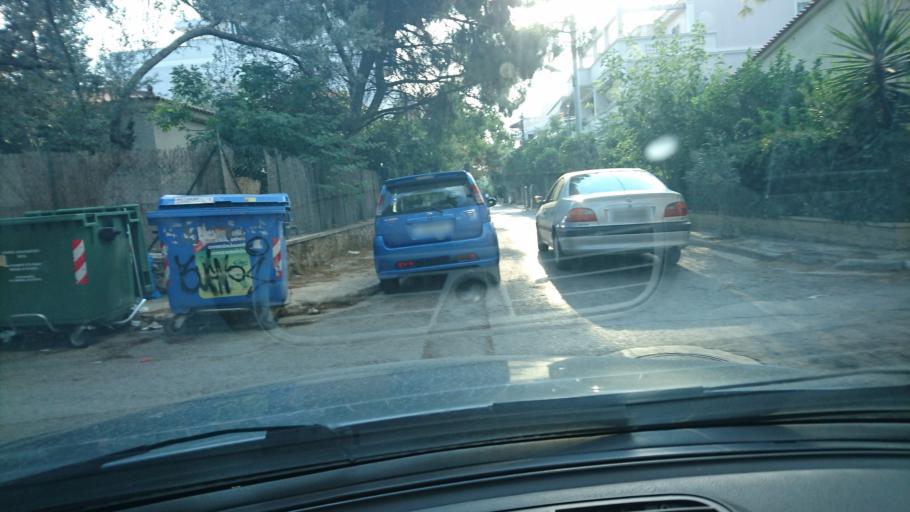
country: GR
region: Attica
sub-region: Nomarchia Athinas
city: Cholargos
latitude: 38.0078
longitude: 23.7974
